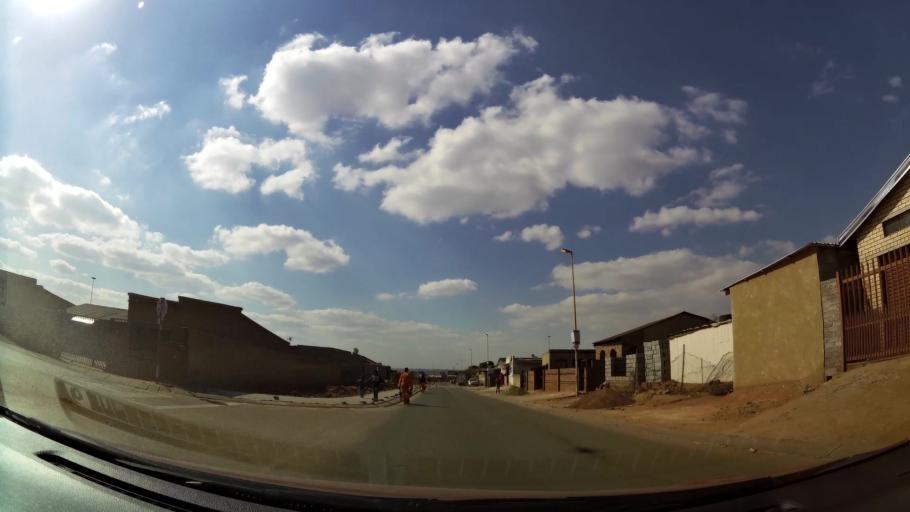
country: ZA
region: Gauteng
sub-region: Ekurhuleni Metropolitan Municipality
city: Tembisa
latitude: -26.0037
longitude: 28.2172
